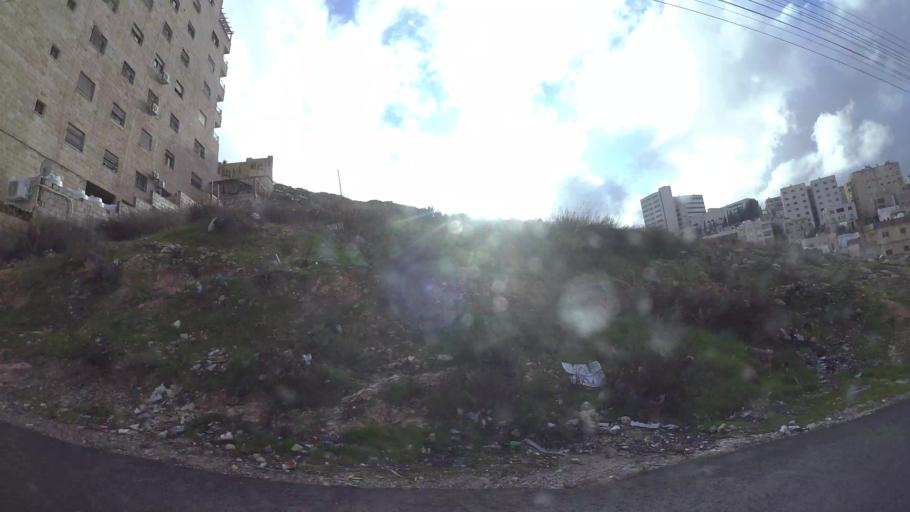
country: JO
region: Amman
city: Amman
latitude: 32.0014
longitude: 35.9232
